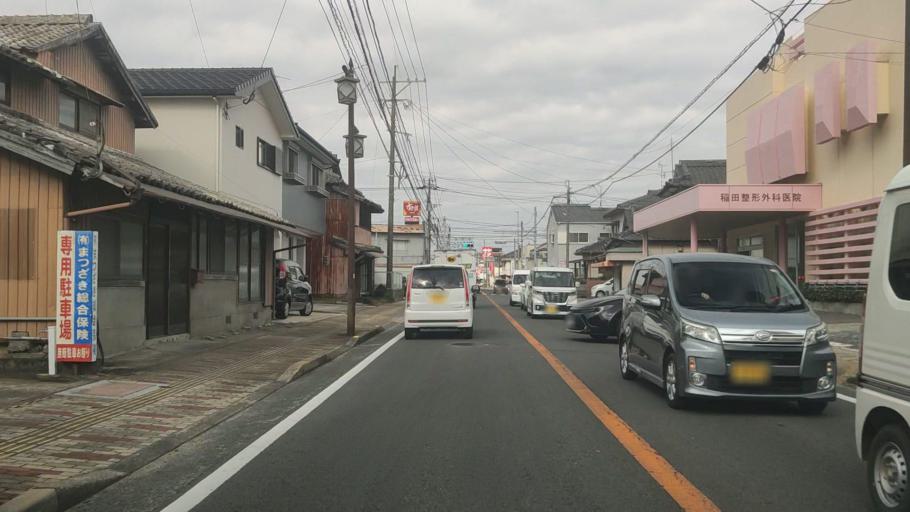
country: JP
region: Nagasaki
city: Shimabara
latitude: 32.7914
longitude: 130.3697
